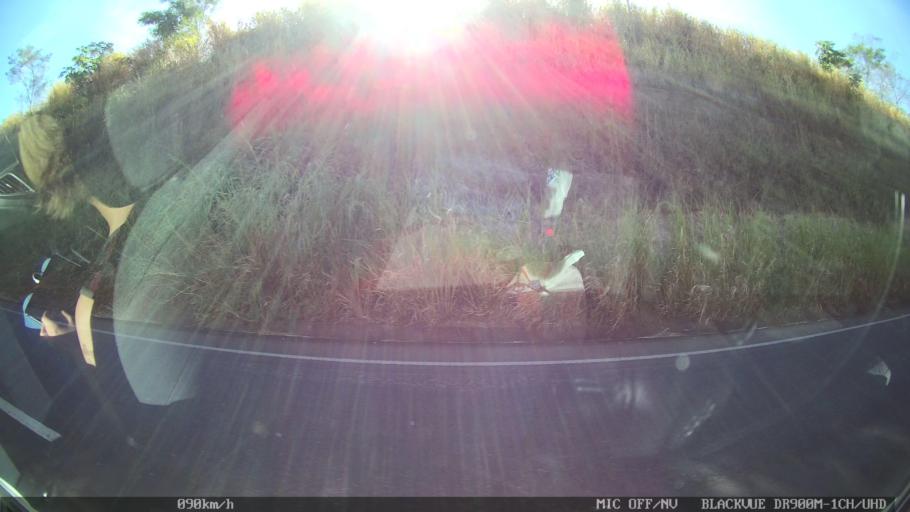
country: BR
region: Sao Paulo
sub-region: Barretos
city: Barretos
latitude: -20.6039
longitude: -48.7351
